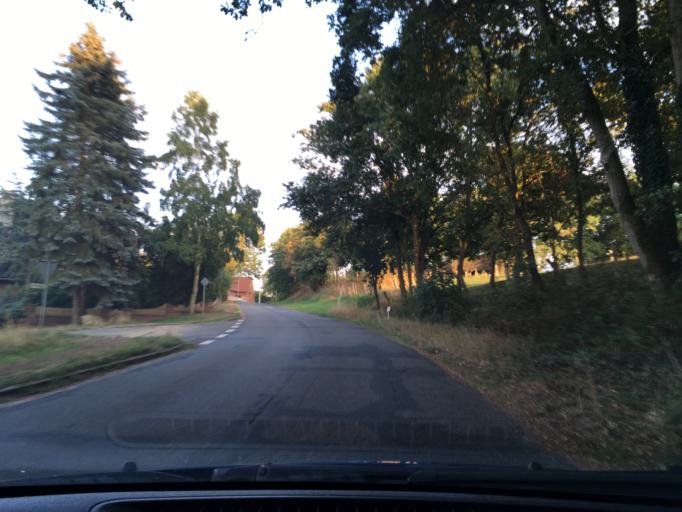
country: DE
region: Lower Saxony
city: Bleckede
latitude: 53.2655
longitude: 10.7037
